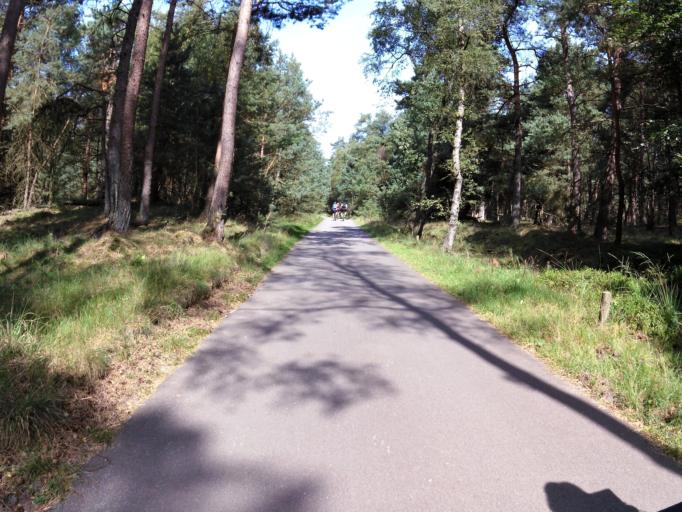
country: NL
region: Gelderland
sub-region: Gemeente Rozendaal
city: Rozendaal
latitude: 52.0350
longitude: 5.9929
